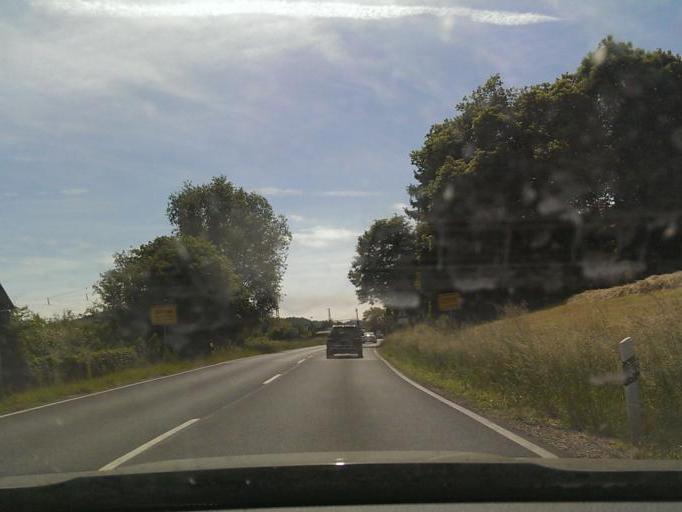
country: DE
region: Lower Saxony
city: Bruggen
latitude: 52.0136
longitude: 9.7873
